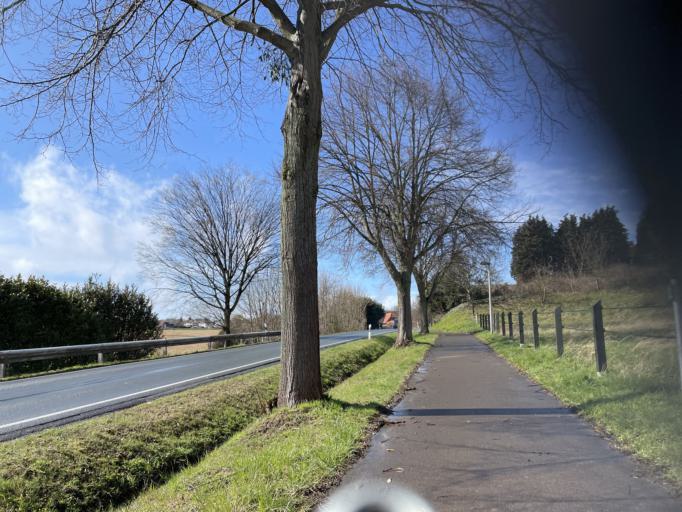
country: DE
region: North Rhine-Westphalia
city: Porta Westfalica
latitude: 52.2297
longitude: 8.9512
